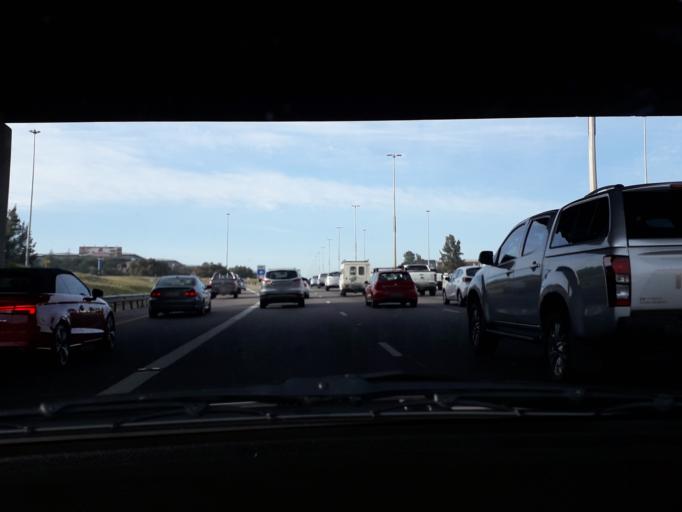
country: ZA
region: Gauteng
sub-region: City of Johannesburg Metropolitan Municipality
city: Midrand
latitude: -25.9540
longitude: 28.1344
